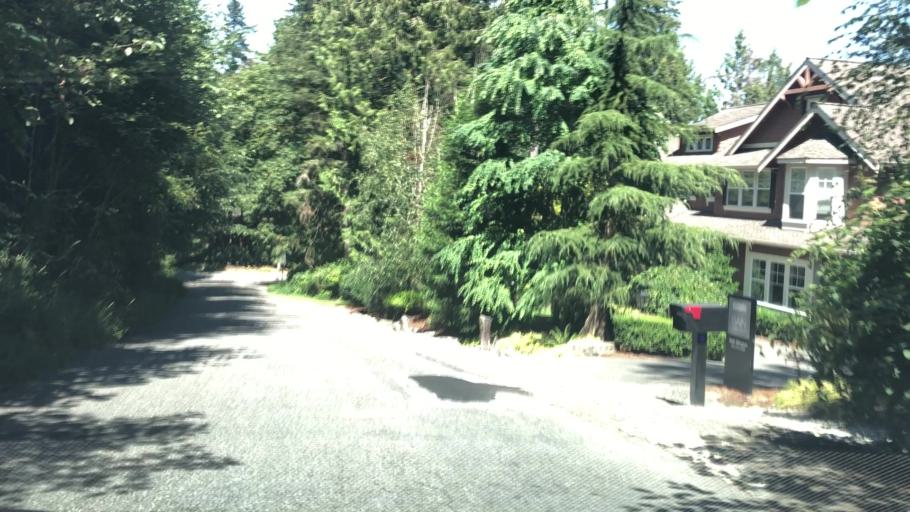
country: US
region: Washington
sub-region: King County
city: Cottage Lake
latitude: 47.7301
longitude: -122.0903
